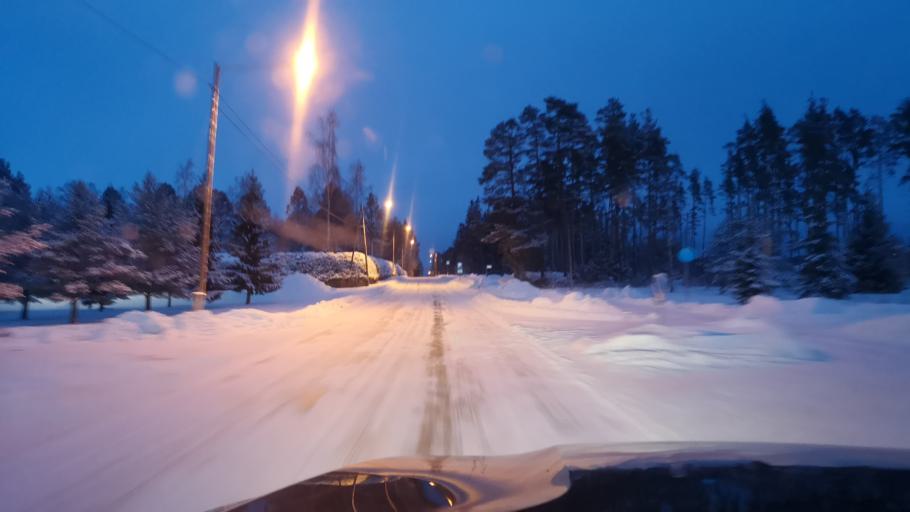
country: FI
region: Varsinais-Suomi
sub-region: Loimaa
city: Loimaa
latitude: 60.8630
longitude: 23.0807
